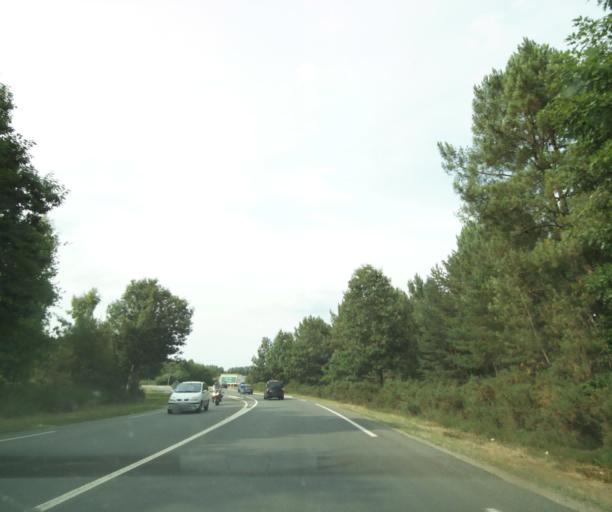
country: FR
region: Pays de la Loire
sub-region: Departement de la Sarthe
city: Mulsanne
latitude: 47.9399
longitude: 0.2364
